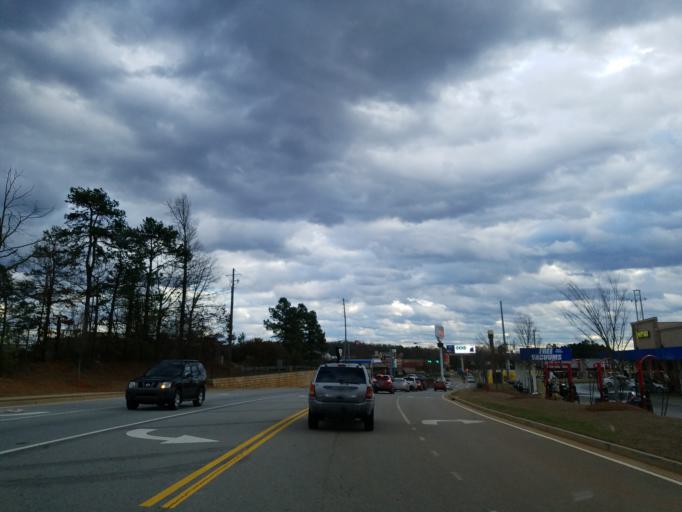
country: US
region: Georgia
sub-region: Henry County
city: Locust Grove
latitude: 33.3550
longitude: -84.1217
